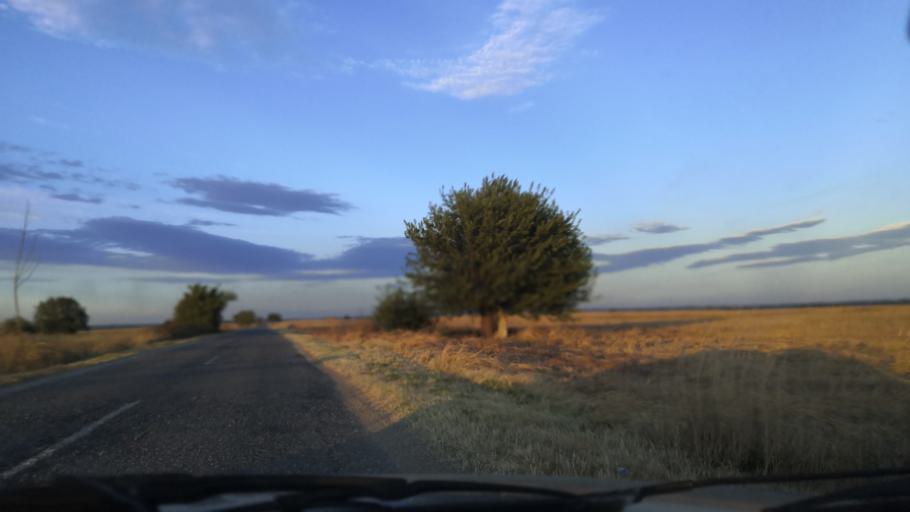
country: RO
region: Mehedinti
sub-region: Comuna Gruia
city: Izvoarele
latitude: 44.2546
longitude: 22.6286
